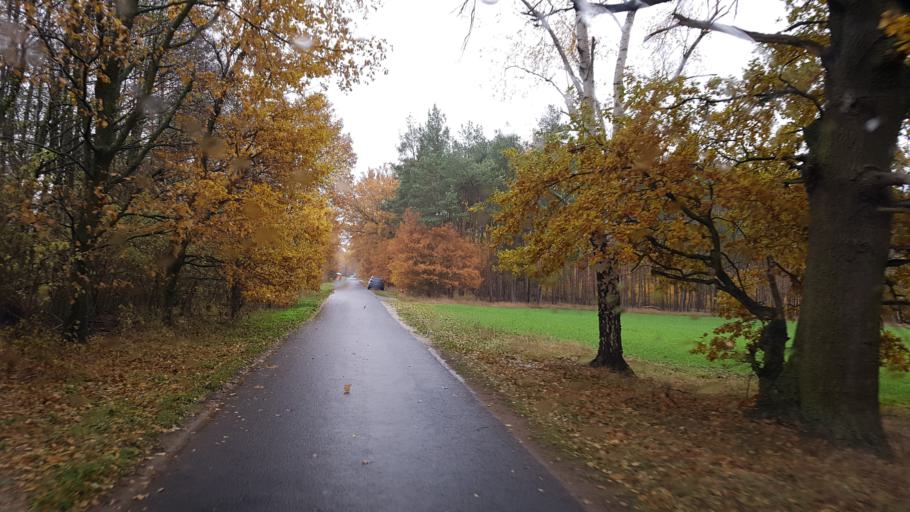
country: DE
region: Brandenburg
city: Herzberg
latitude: 51.6433
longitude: 13.2157
